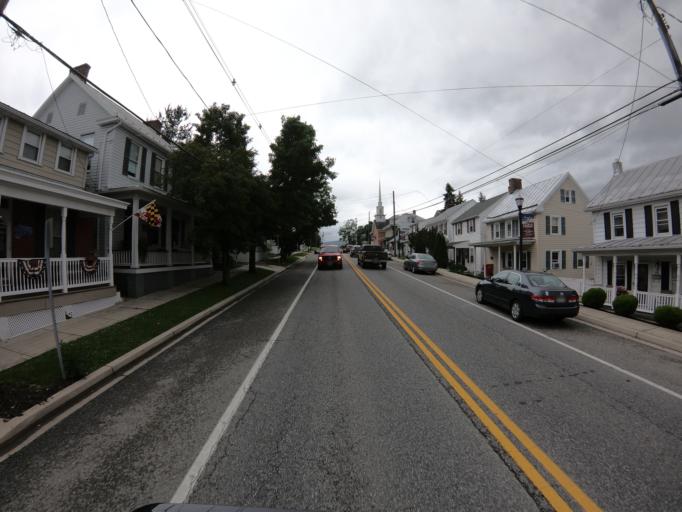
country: US
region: Maryland
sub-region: Washington County
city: Boonsboro
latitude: 39.5043
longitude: -77.6510
